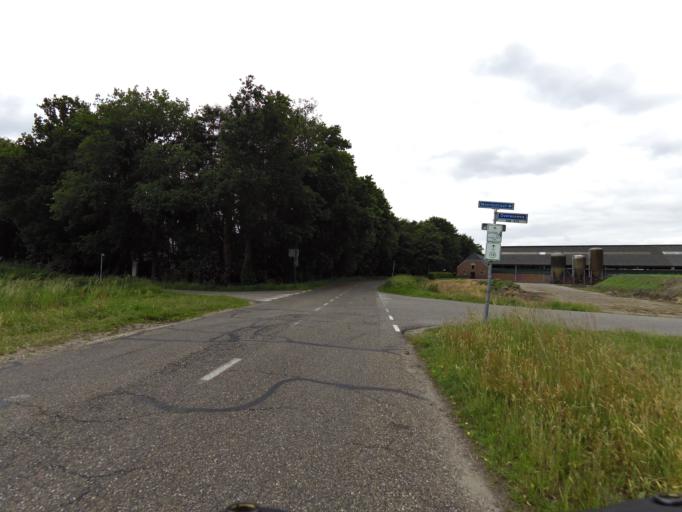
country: NL
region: North Brabant
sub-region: Gemeente Breda
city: Breda
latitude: 51.5314
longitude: 4.7385
